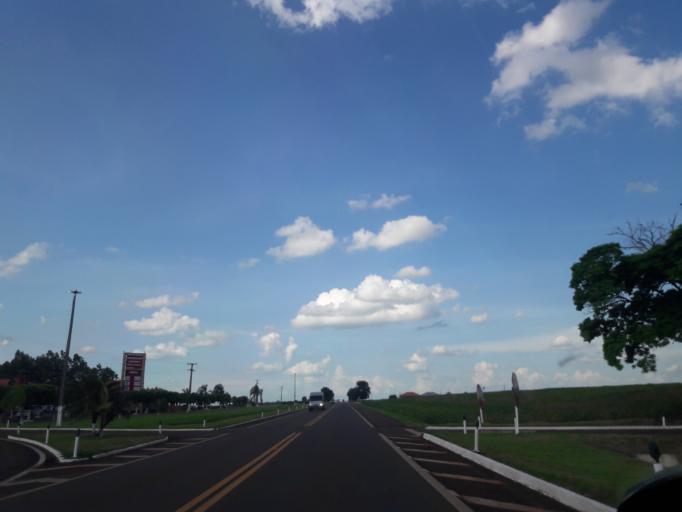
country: BR
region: Parana
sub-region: Moreira Sales
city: Moreira Sales
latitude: -24.4105
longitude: -52.8178
